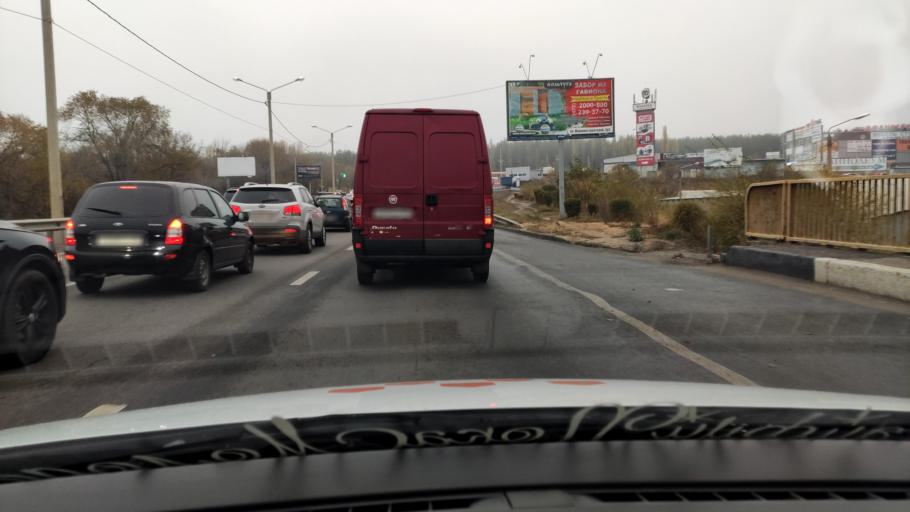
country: RU
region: Voronezj
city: Pridonskoy
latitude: 51.6700
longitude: 39.1228
